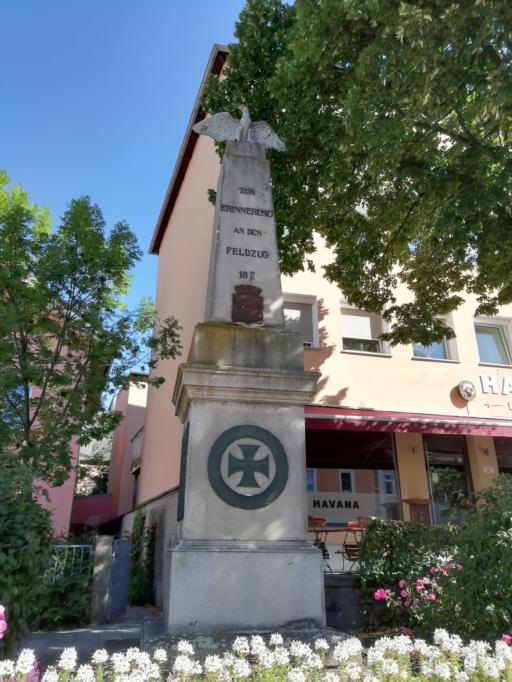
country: DE
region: Bavaria
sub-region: Upper Palatinate
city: Cham
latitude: 49.2197
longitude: 12.6631
